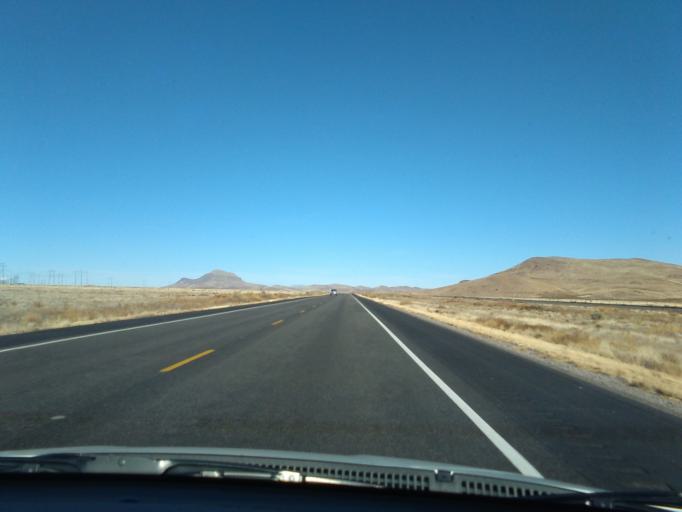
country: US
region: New Mexico
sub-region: Dona Ana County
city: Hatch
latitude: 32.5252
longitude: -107.4936
